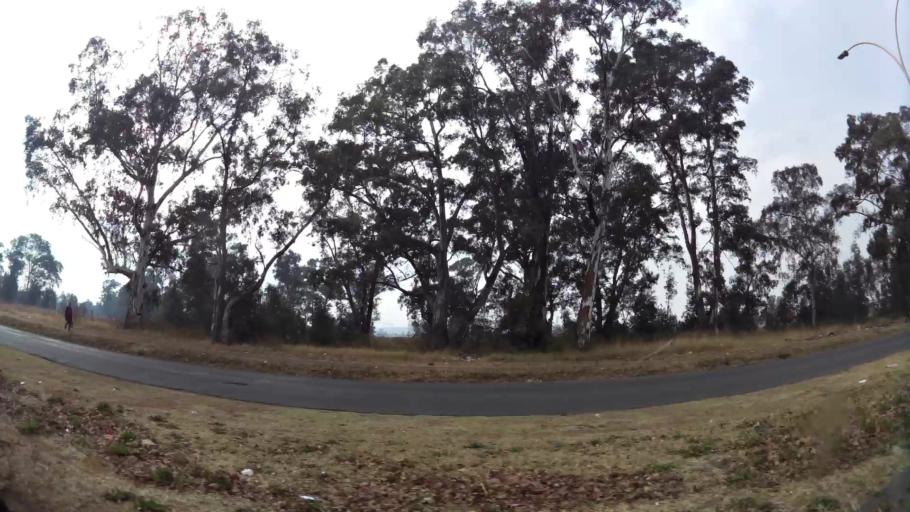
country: ZA
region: Gauteng
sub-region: Sedibeng District Municipality
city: Vanderbijlpark
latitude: -26.6767
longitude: 27.8377
